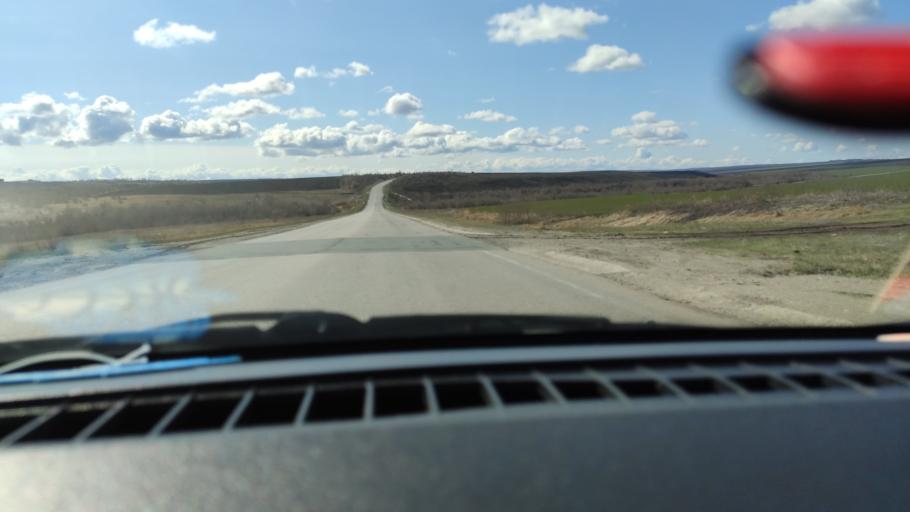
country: RU
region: Samara
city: Varlamovo
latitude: 53.0714
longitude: 48.3541
